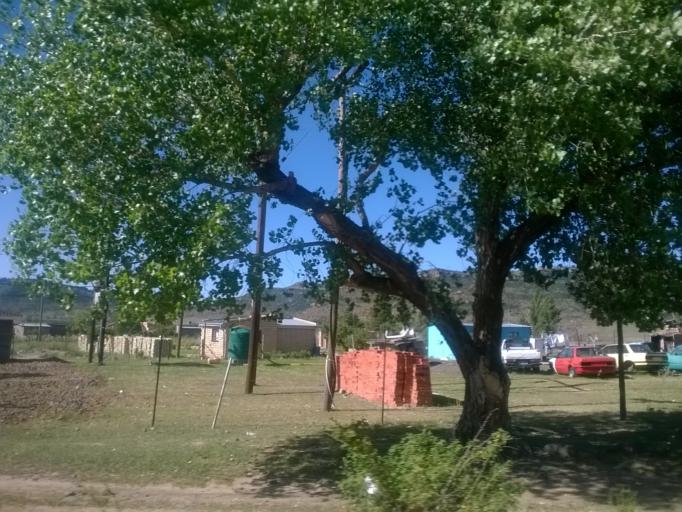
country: LS
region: Maseru
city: Maseru
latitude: -29.2672
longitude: 27.5761
